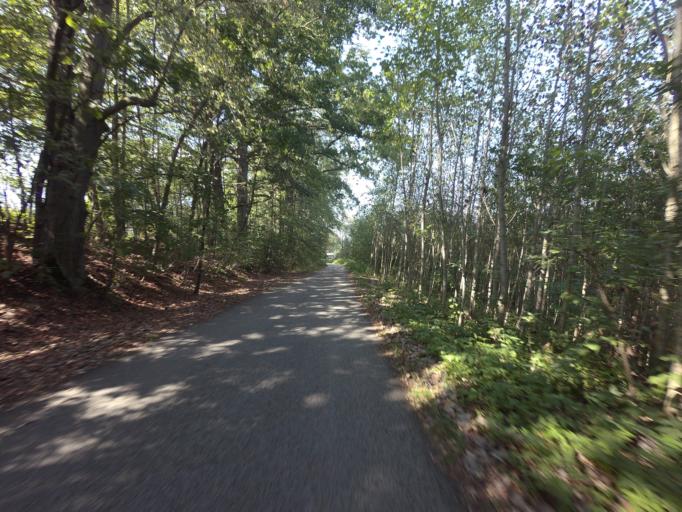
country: CZ
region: Jihocesky
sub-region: Okres Ceske Budejovice
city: Hluboka nad Vltavou
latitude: 49.1226
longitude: 14.4564
